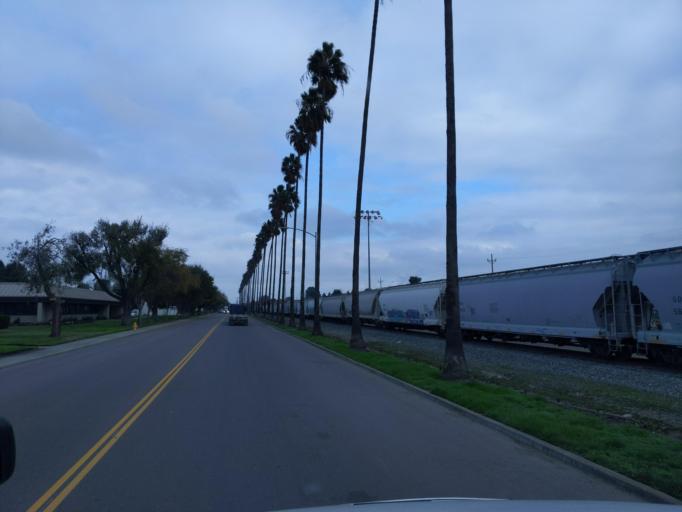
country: US
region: California
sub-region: San Joaquin County
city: Country Club
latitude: 37.9490
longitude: -121.3541
